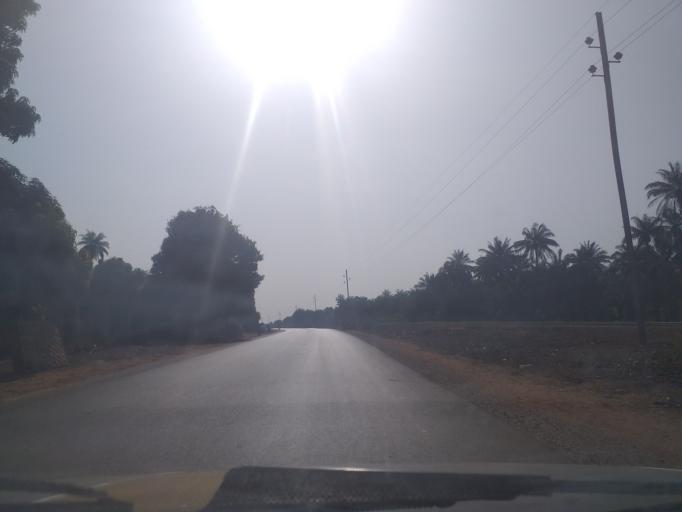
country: GN
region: Boke
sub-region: Boke Prefecture
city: Sangueya
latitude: 10.7774
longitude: -14.4383
